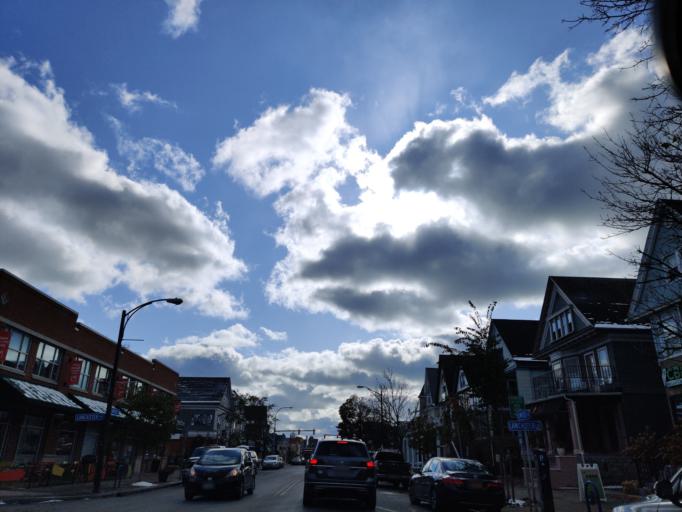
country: US
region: New York
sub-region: Erie County
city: Buffalo
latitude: 42.9196
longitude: -78.8770
